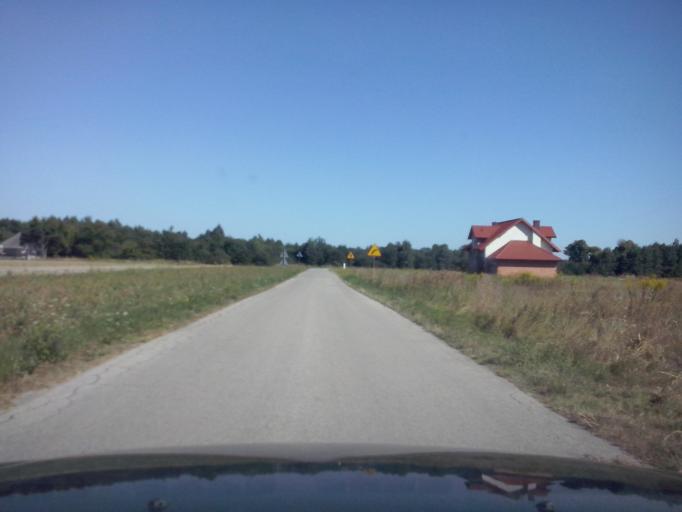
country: PL
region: Swietokrzyskie
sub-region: Powiat kielecki
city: Chmielnik
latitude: 50.6129
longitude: 20.7112
